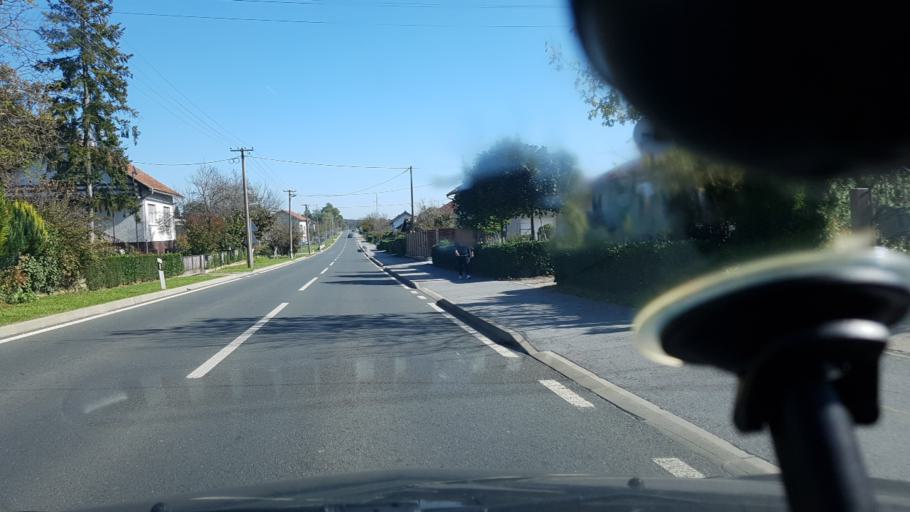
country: HR
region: Zagrebacka
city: Kriz
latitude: 45.7131
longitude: 16.4411
